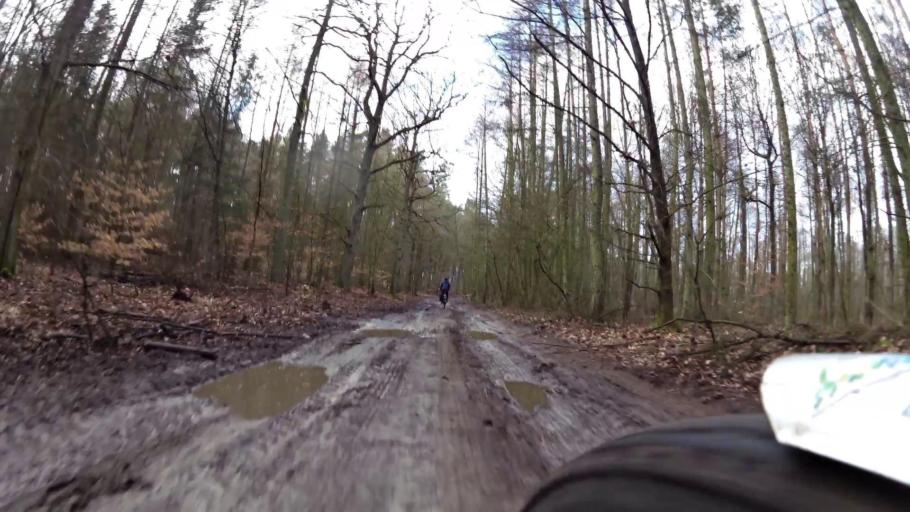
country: PL
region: West Pomeranian Voivodeship
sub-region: Powiat kamienski
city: Wolin
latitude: 53.8654
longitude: 14.7117
